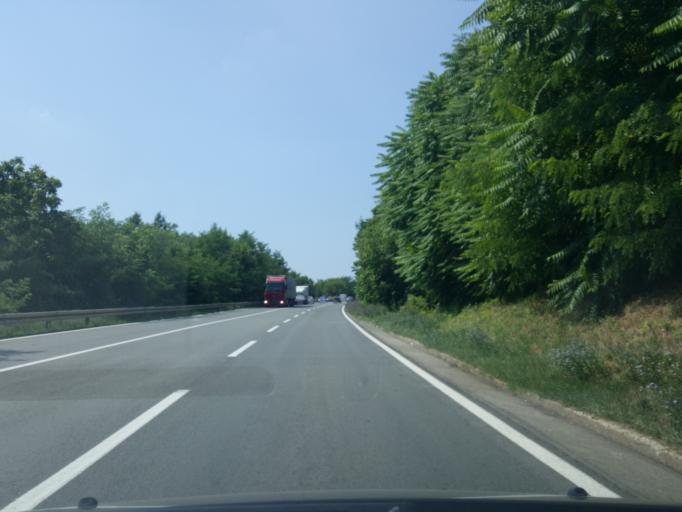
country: RS
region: Central Serbia
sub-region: Belgrade
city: Sopot
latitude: 44.5522
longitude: 20.6655
